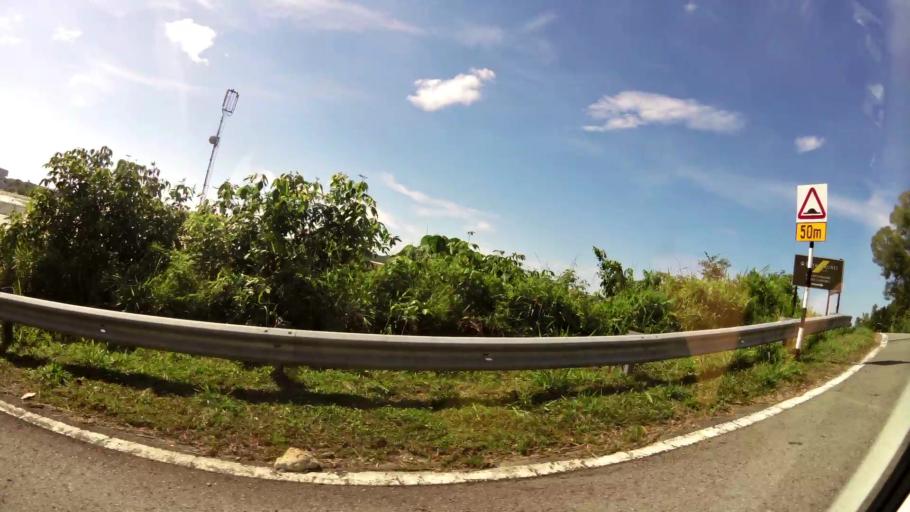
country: BN
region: Brunei and Muara
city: Bandar Seri Begawan
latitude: 4.9510
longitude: 114.9369
